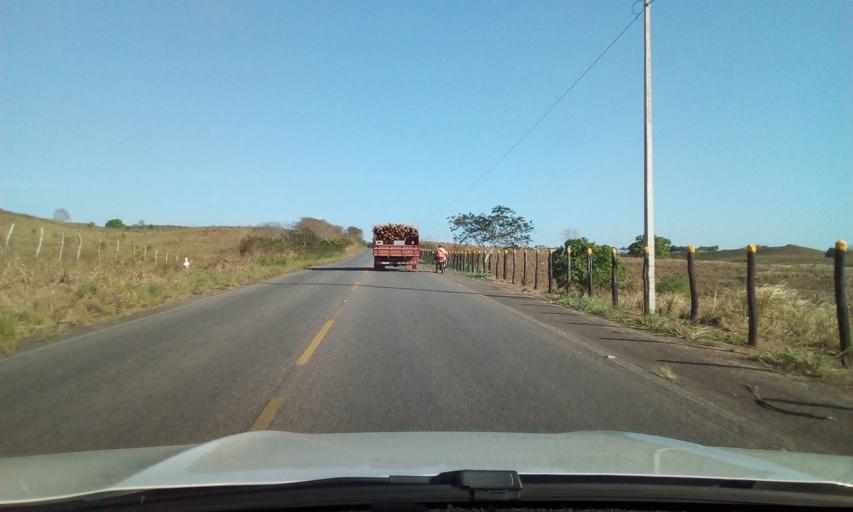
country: BR
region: Paraiba
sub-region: Mari
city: Mari
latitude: -7.0111
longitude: -35.3633
